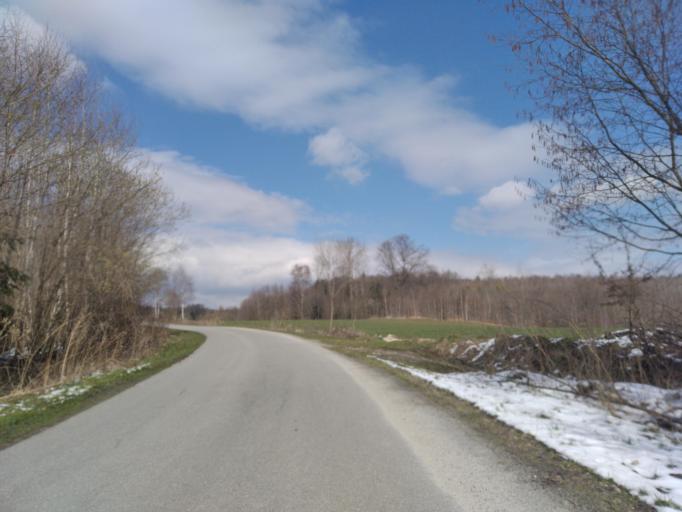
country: PL
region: Subcarpathian Voivodeship
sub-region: Powiat ropczycko-sedziszowski
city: Ropczyce
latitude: 50.0100
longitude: 21.5860
